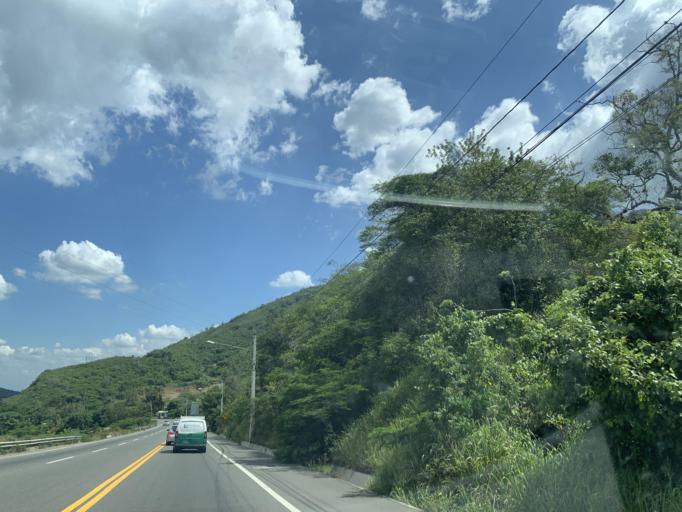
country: DO
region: Santiago
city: Villa Bisono
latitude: 19.6147
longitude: -70.8408
